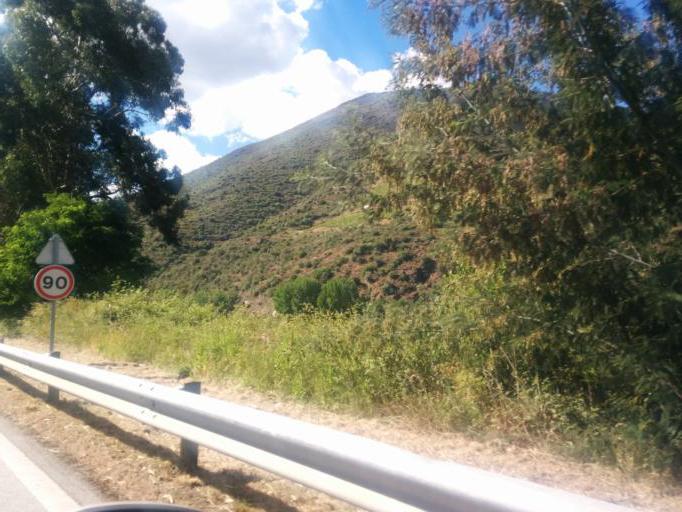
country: PT
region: Viseu
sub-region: Armamar
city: Armamar
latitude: 41.1415
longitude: -7.7034
